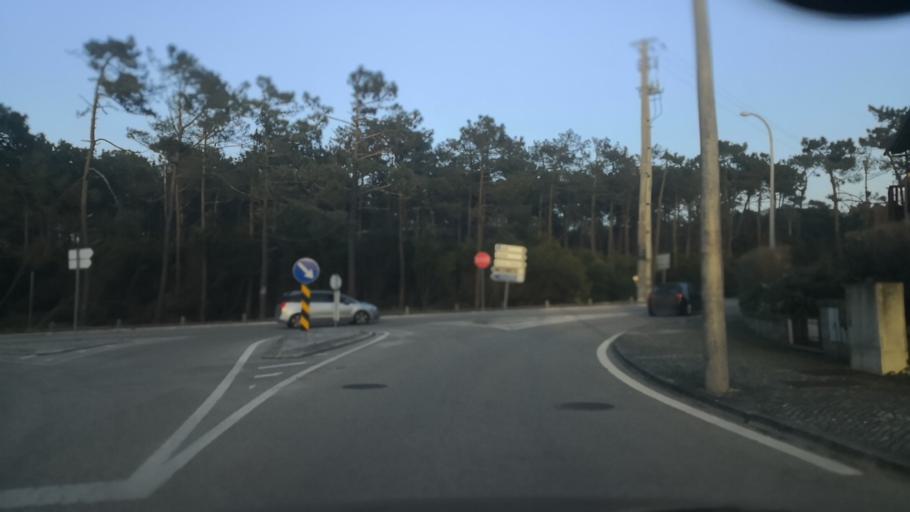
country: PT
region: Leiria
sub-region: Alcobaca
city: Pataias
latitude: 39.7552
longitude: -9.0256
